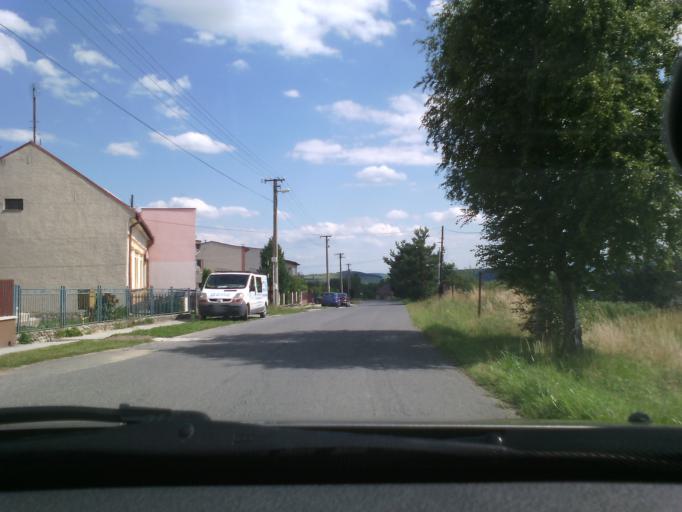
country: SK
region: Presovsky
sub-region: Okres Poprad
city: Nova Lesna
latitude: 49.1348
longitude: 20.3110
